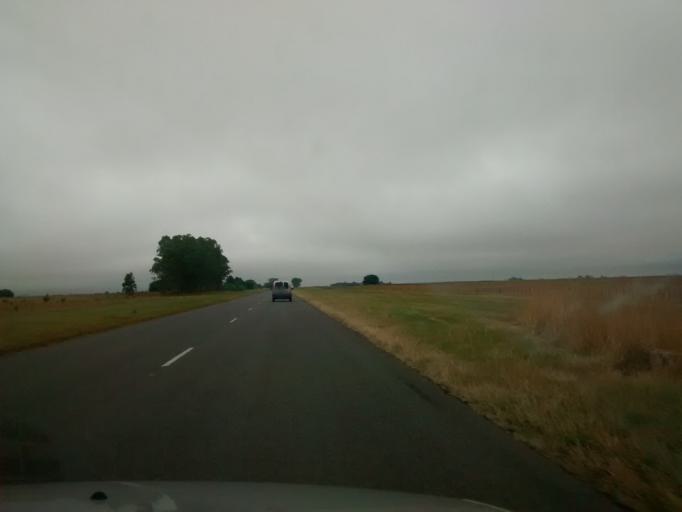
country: AR
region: Buenos Aires
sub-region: Partido de Ayacucho
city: Ayacucho
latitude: -37.2378
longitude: -58.4916
